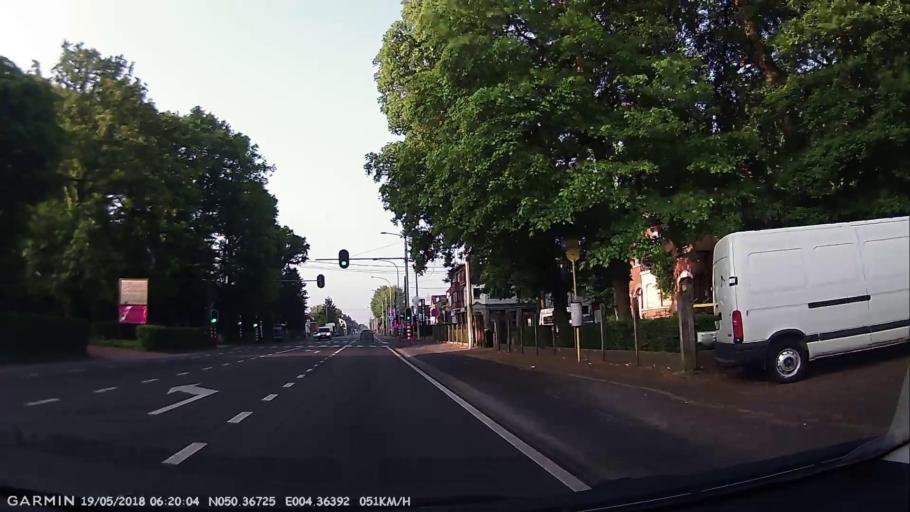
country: BE
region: Wallonia
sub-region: Province du Hainaut
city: Thuin
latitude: 50.3672
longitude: 4.3639
